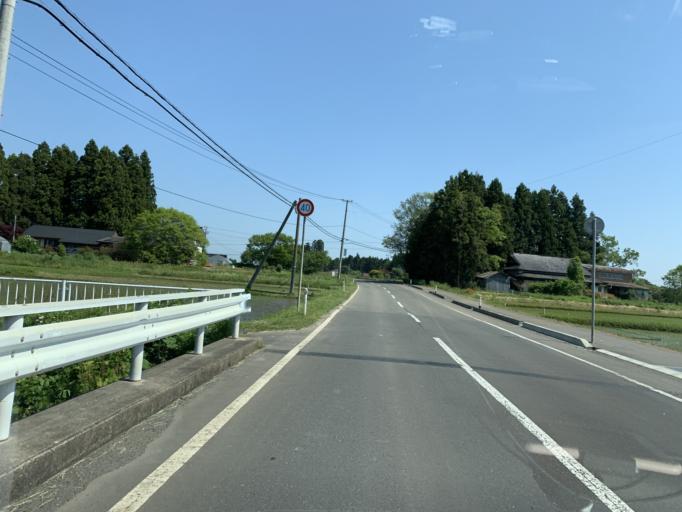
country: JP
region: Iwate
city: Mizusawa
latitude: 39.0961
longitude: 141.0754
